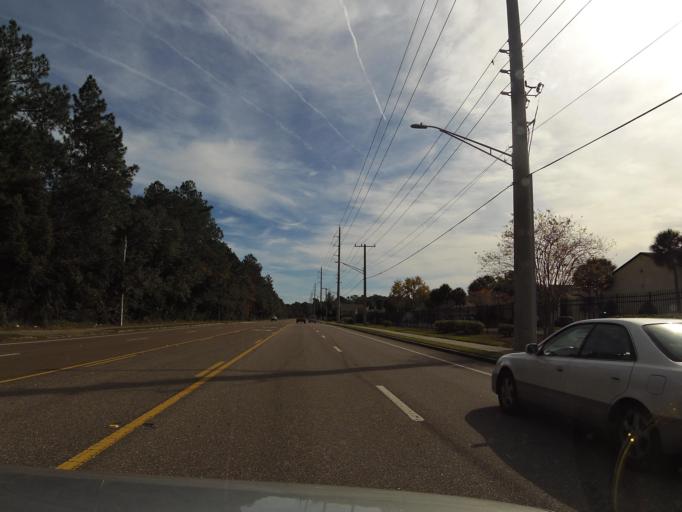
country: US
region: Florida
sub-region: Duval County
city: Jacksonville
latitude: 30.2484
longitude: -81.6125
